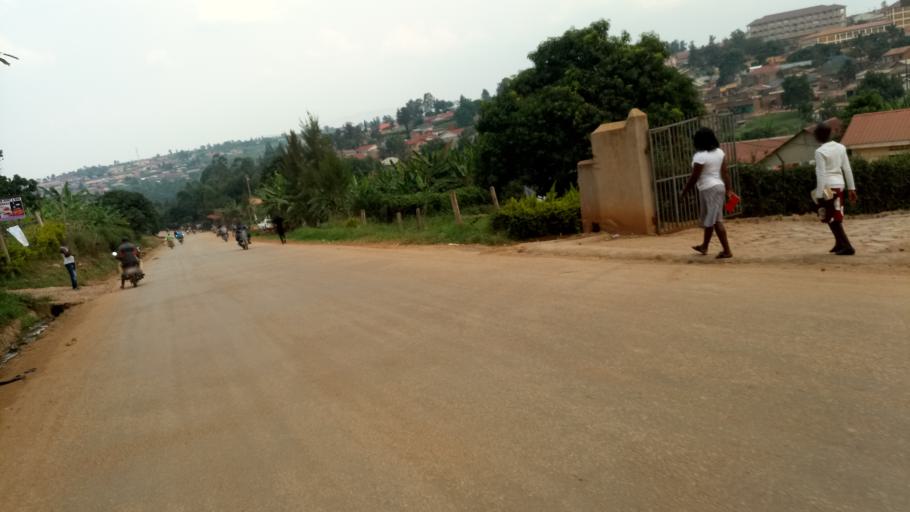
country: UG
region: Western Region
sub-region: Mbarara District
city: Mbarara
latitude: -0.6101
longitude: 30.6640
